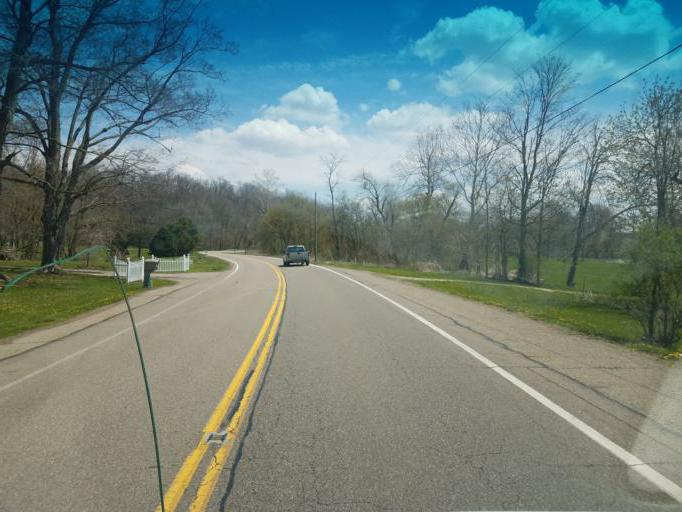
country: US
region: Ohio
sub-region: Knox County
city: Danville
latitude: 40.4064
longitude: -82.3116
